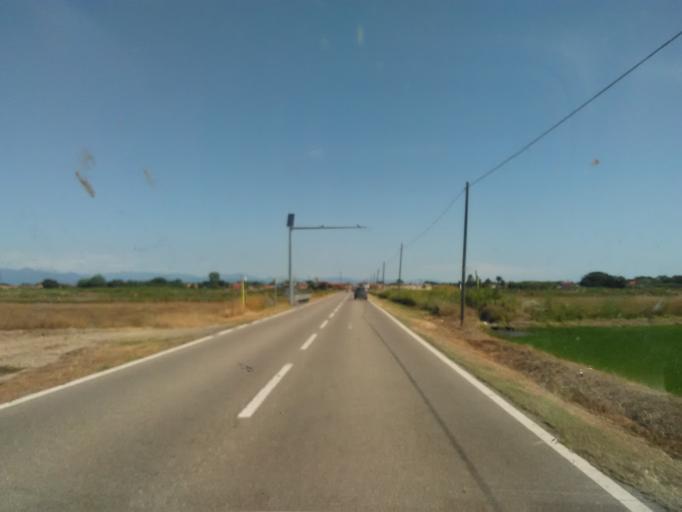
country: IT
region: Piedmont
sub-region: Provincia di Vercelli
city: Greggio
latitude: 45.4436
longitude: 8.3838
